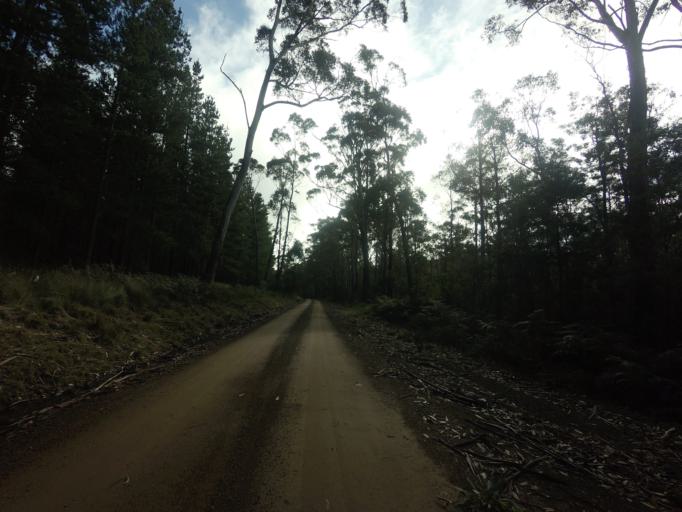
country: AU
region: Tasmania
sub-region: Derwent Valley
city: New Norfolk
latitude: -42.7660
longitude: 146.8988
